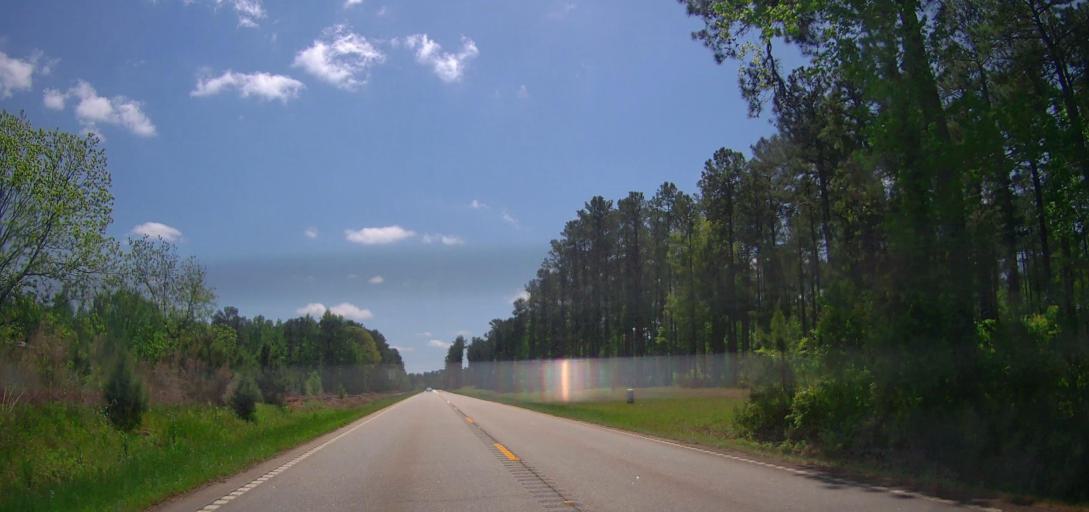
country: US
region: Georgia
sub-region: Jasper County
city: Monticello
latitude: 33.1624
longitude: -83.6424
